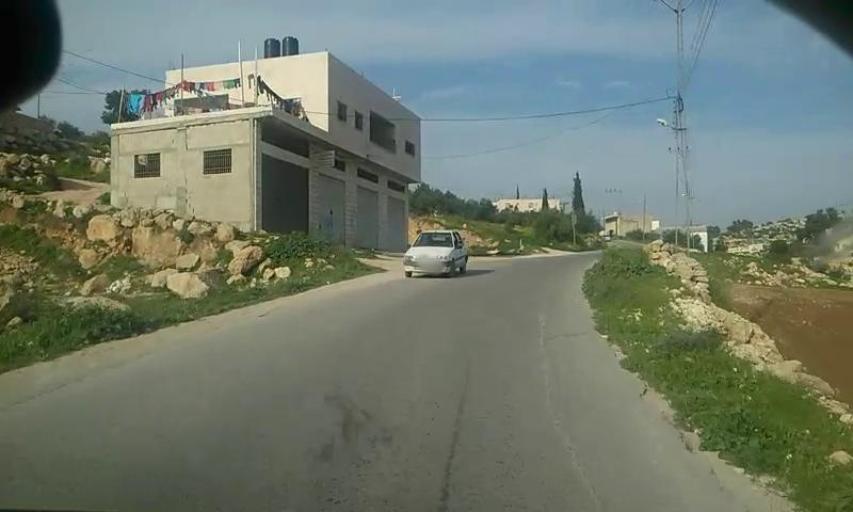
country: PS
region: West Bank
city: Bayt Ula
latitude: 31.5865
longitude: 35.0236
